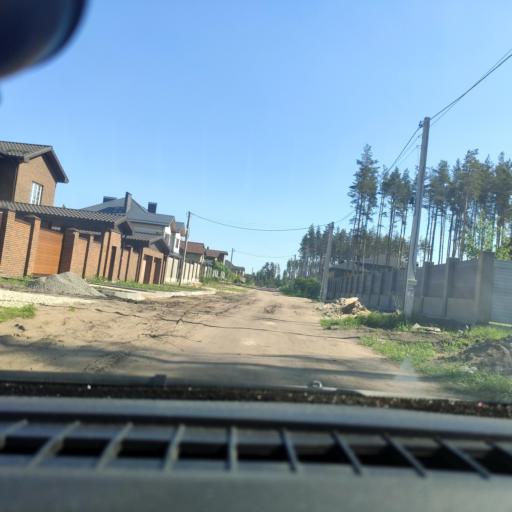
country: RU
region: Voronezj
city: Podgornoye
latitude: 51.7798
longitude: 39.1458
